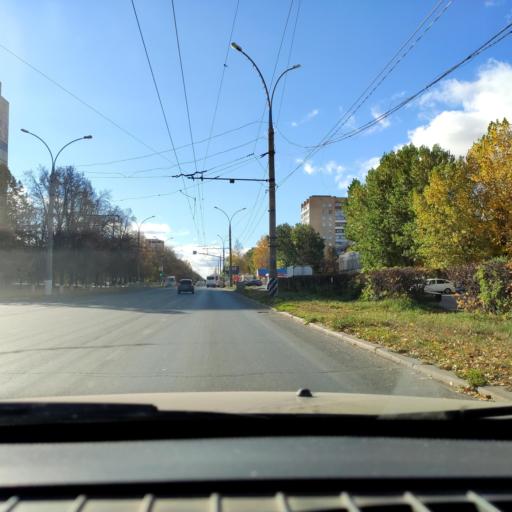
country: RU
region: Samara
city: Tol'yatti
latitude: 53.5375
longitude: 49.2782
